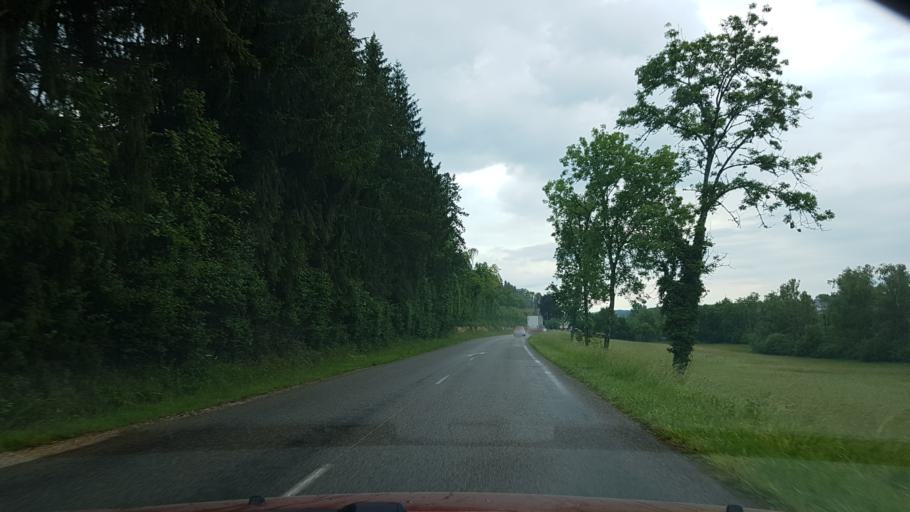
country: FR
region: Franche-Comte
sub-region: Departement du Jura
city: Clairvaux-les-Lacs
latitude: 46.5668
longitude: 5.7444
